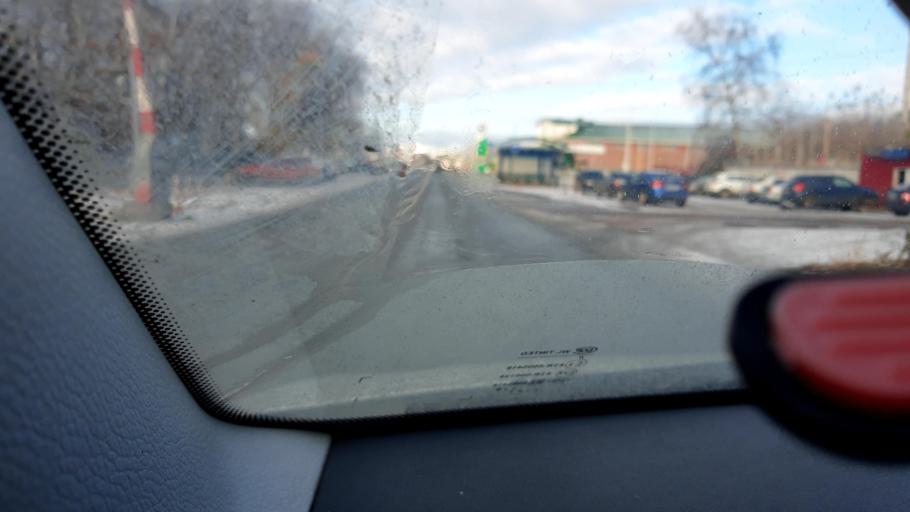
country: RU
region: Bashkortostan
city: Ufa
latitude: 54.8034
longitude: 56.0988
